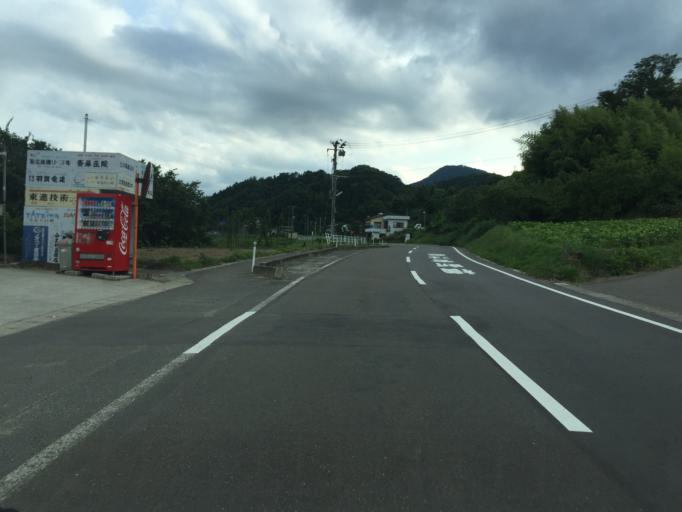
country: JP
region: Fukushima
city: Hobaramachi
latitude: 37.7254
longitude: 140.5970
